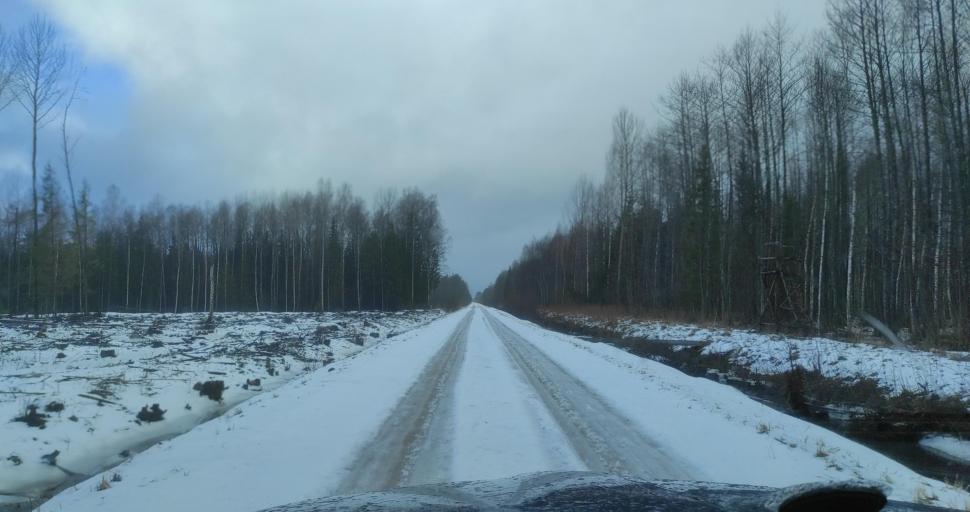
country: LV
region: Dundaga
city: Dundaga
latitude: 57.3937
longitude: 22.1244
